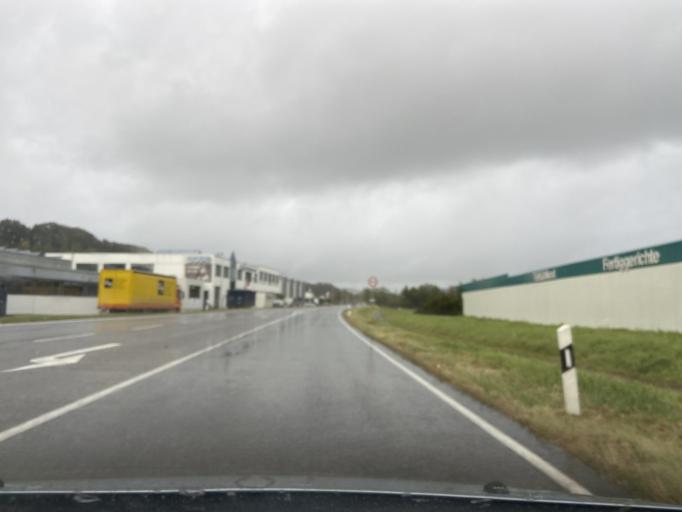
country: DE
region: Baden-Wuerttemberg
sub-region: Tuebingen Region
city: Scheer
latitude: 48.0612
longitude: 9.3008
